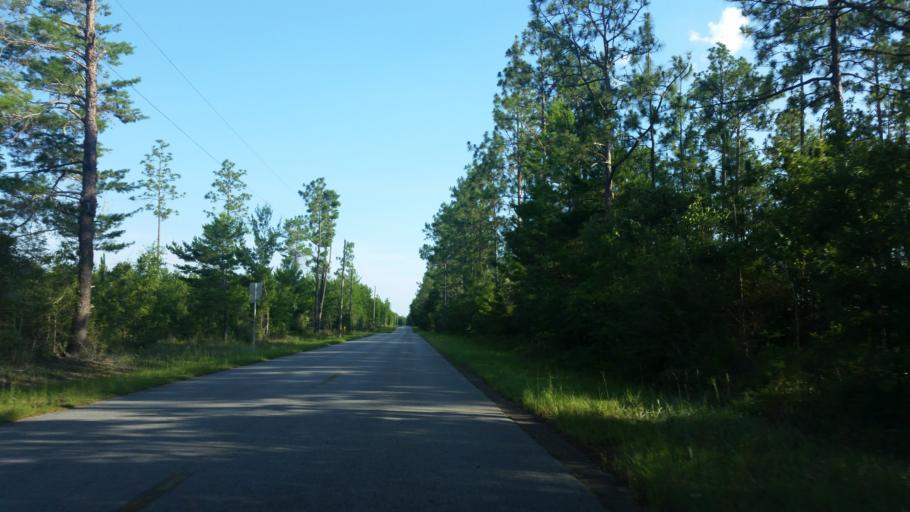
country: US
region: Florida
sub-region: Santa Rosa County
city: East Milton
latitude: 30.6832
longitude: -86.8764
